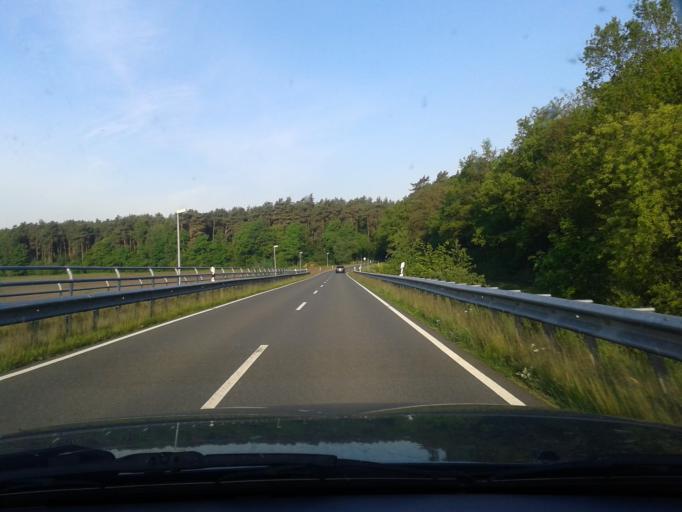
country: DE
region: Lower Saxony
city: Adelheidsdorf
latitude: 52.5526
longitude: 10.0670
